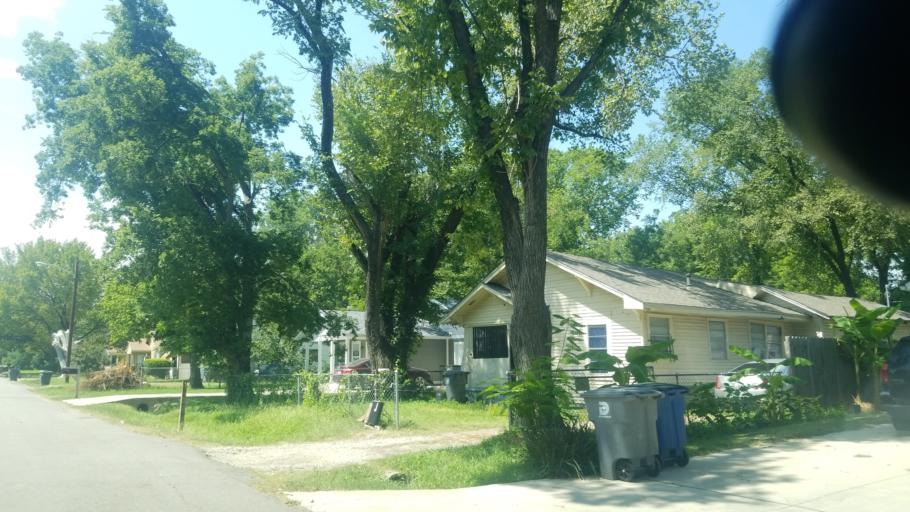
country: US
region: Texas
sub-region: Dallas County
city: Hutchins
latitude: 32.7133
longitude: -96.7456
